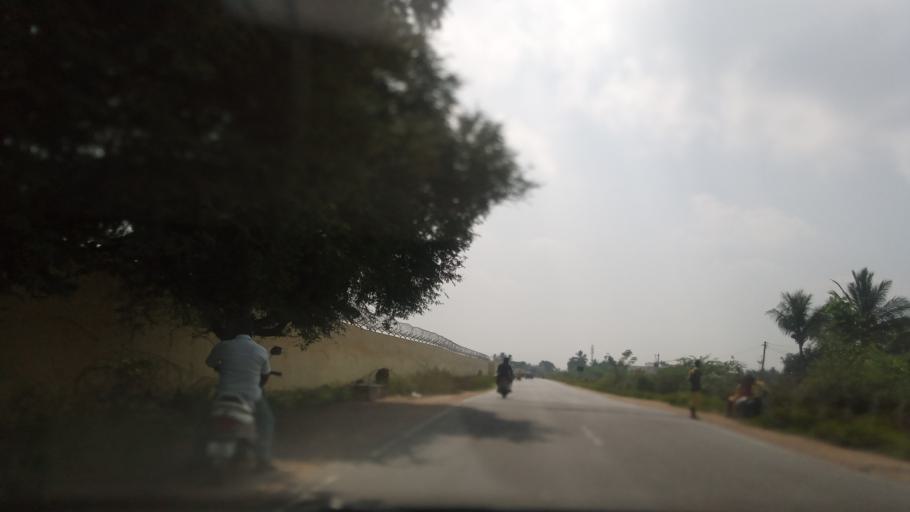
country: IN
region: Tamil Nadu
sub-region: Vellore
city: Arakkonam
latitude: 13.0625
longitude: 79.6736
